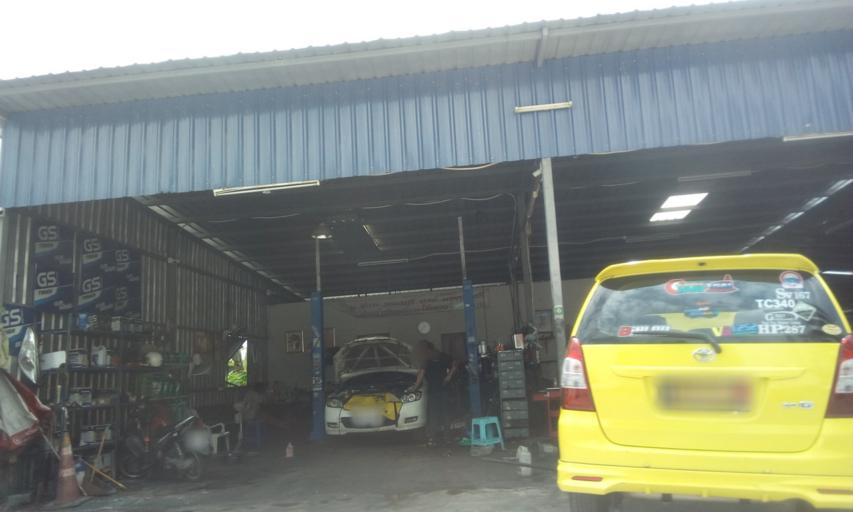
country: TH
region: Bangkok
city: Don Mueang
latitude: 13.9122
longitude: 100.5569
